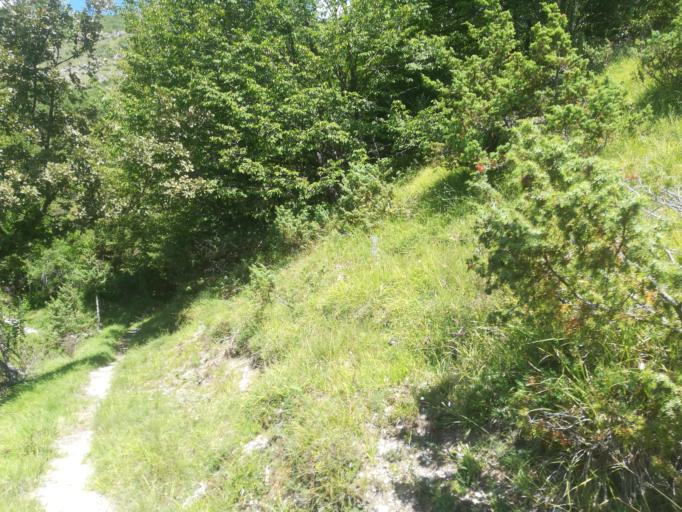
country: IT
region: Umbria
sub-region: Provincia di Perugia
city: Scheggino
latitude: 42.6744
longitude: 12.8584
